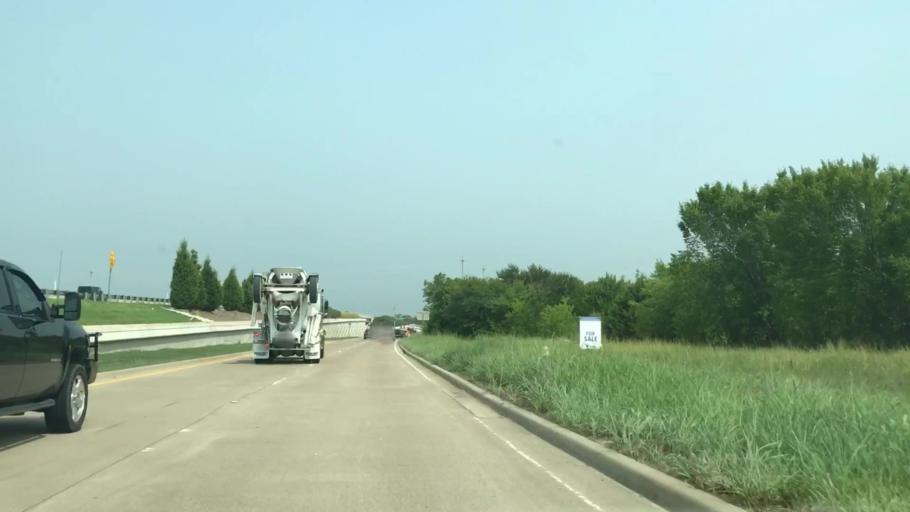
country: US
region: Texas
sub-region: Dallas County
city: Sachse
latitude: 32.9509
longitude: -96.5738
